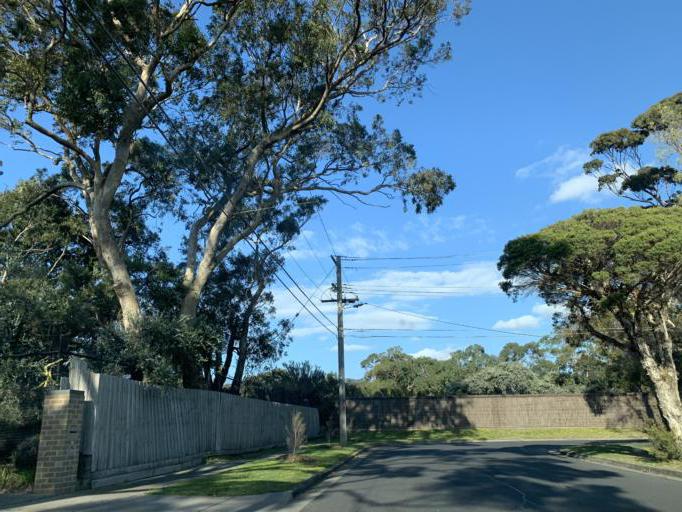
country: AU
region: Victoria
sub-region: Kingston
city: Mordialloc
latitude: -37.9952
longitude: 145.0965
